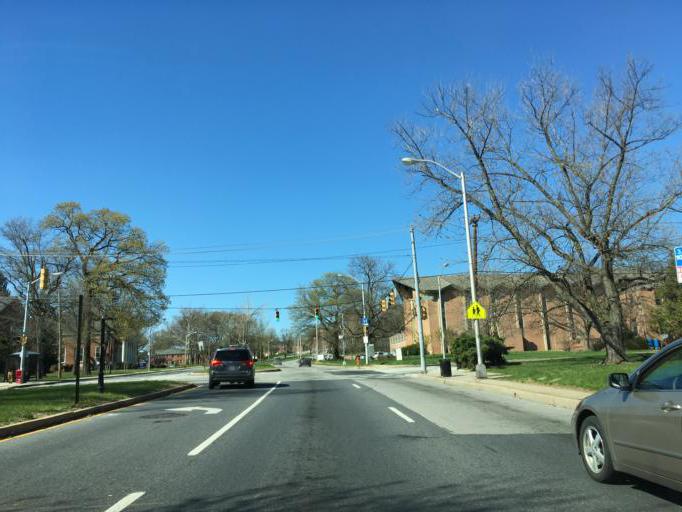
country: US
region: Maryland
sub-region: Baltimore County
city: Towson
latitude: 39.3549
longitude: -76.5896
